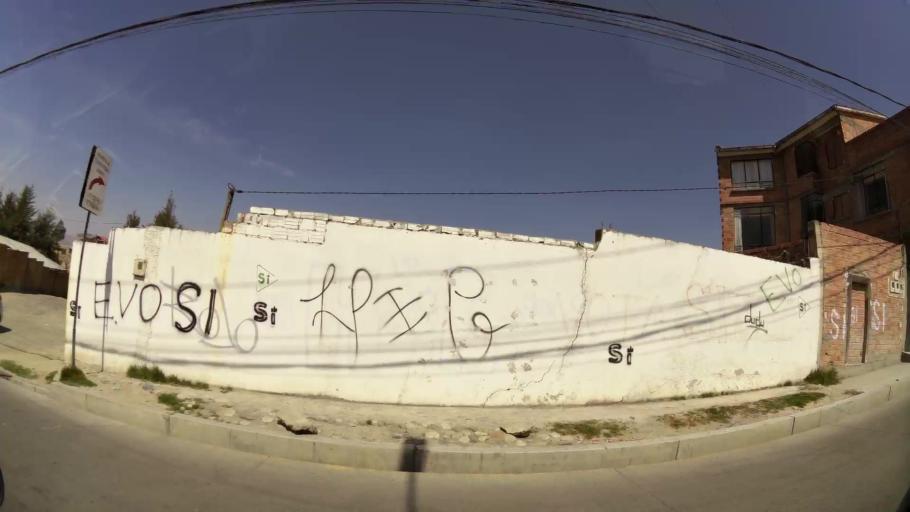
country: BO
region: La Paz
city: La Paz
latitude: -16.5221
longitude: -68.1184
